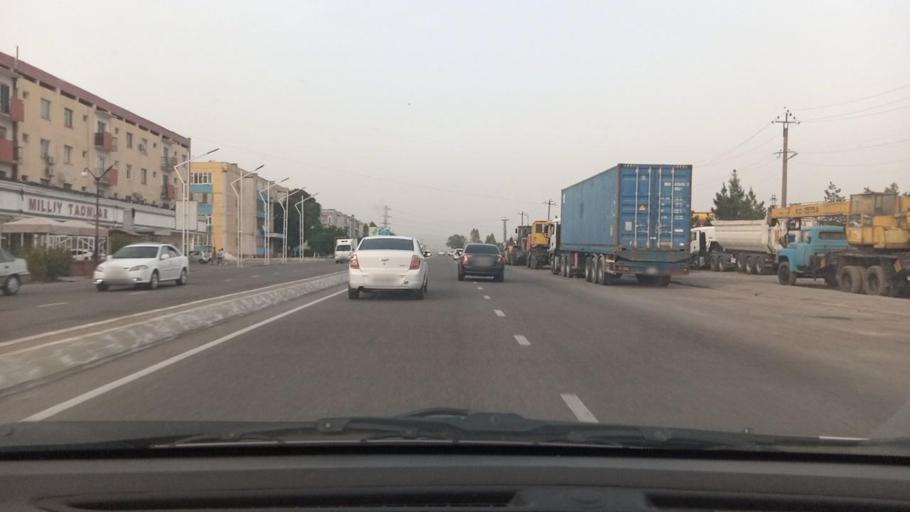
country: UZ
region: Toshkent
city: Angren
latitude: 41.0096
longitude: 70.0967
